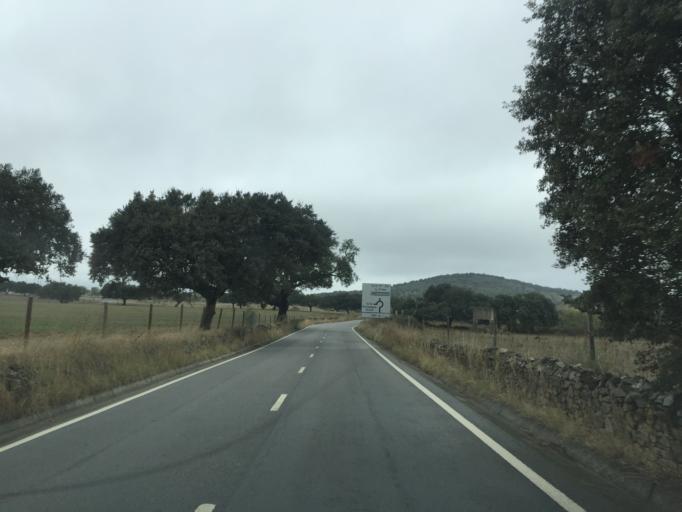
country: PT
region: Portalegre
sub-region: Alter do Chao
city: Alter do Chao
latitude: 39.2187
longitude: -7.6537
